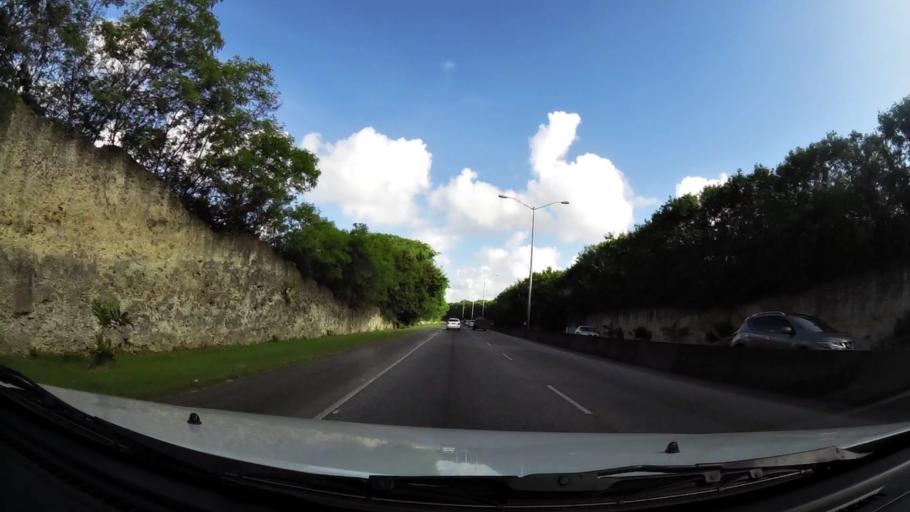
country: BB
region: Saint Michael
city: Bridgetown
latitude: 13.1345
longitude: -59.6001
